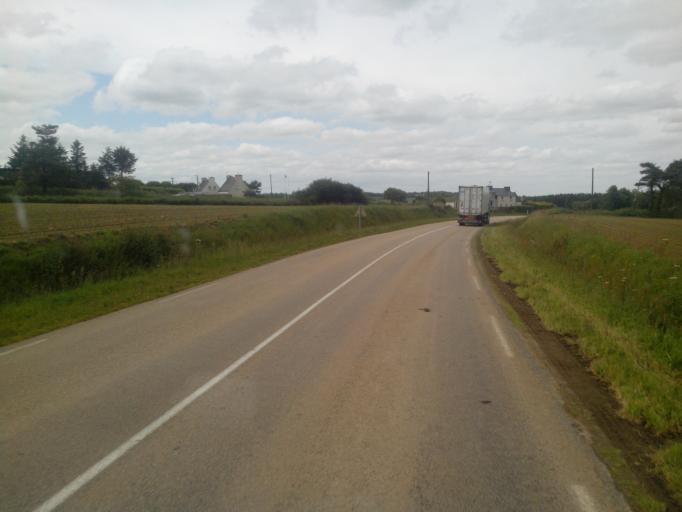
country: FR
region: Brittany
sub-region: Departement du Finistere
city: Guerlesquin
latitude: 48.5291
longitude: -3.5981
